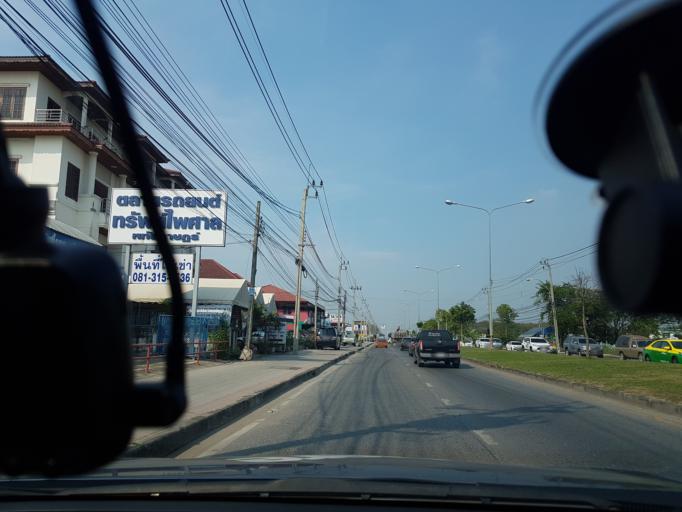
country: TH
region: Bangkok
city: Khlong Sam Wa
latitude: 13.8652
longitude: 100.7225
